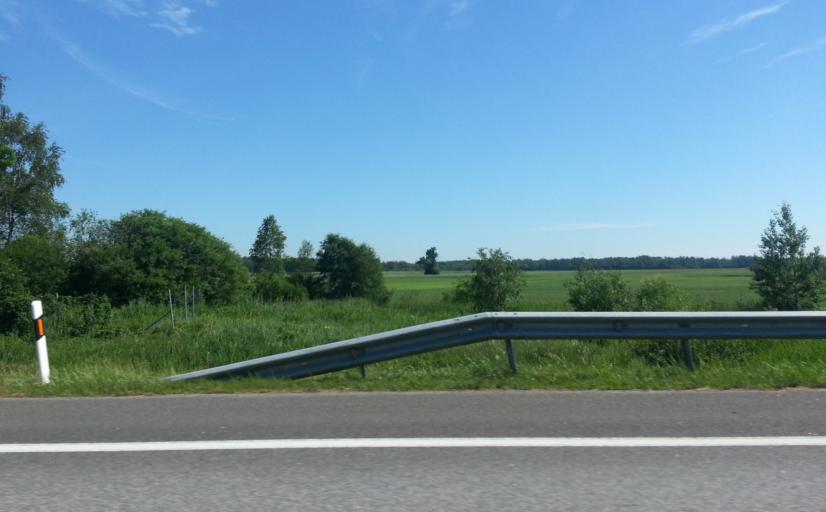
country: LT
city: Ramygala
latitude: 55.5625
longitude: 24.4957
